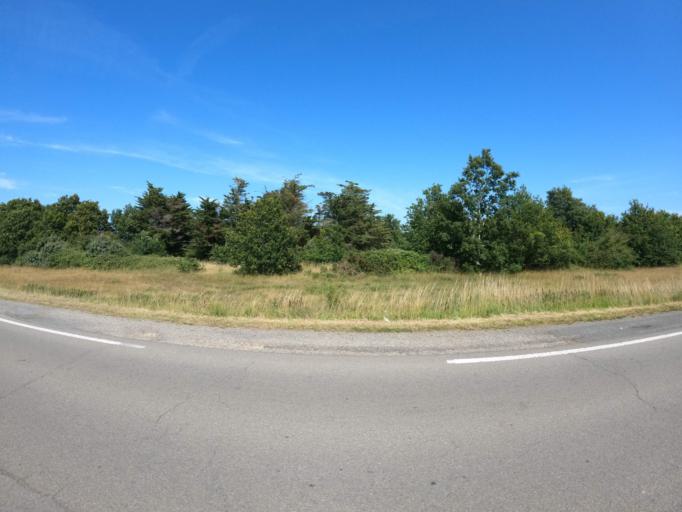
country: FR
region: Pays de la Loire
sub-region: Departement de la Loire-Atlantique
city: La Bernerie-en-Retz
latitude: 47.0969
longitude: -2.0367
